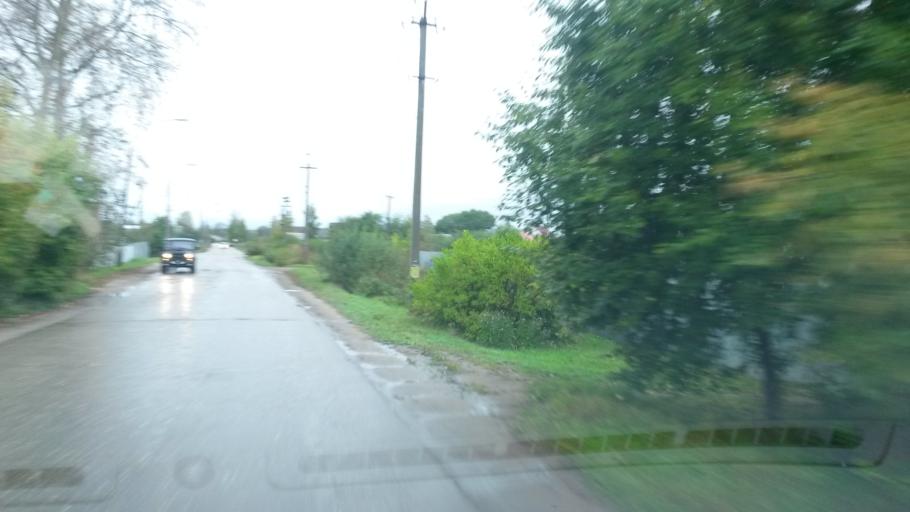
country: RU
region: Jaroslavl
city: Gavrilov-Yam
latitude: 57.3113
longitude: 39.8582
